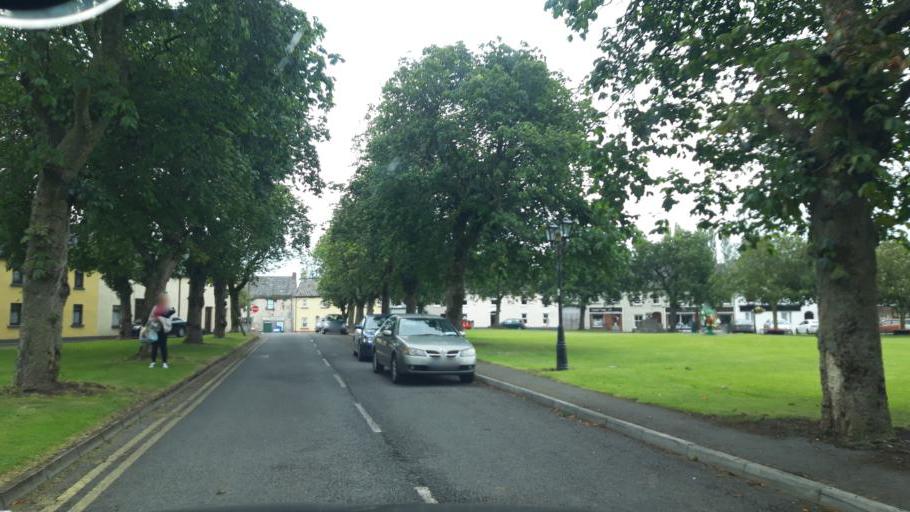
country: IE
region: Leinster
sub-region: Kilkenny
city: Ballyragget
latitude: 52.7317
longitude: -7.3988
